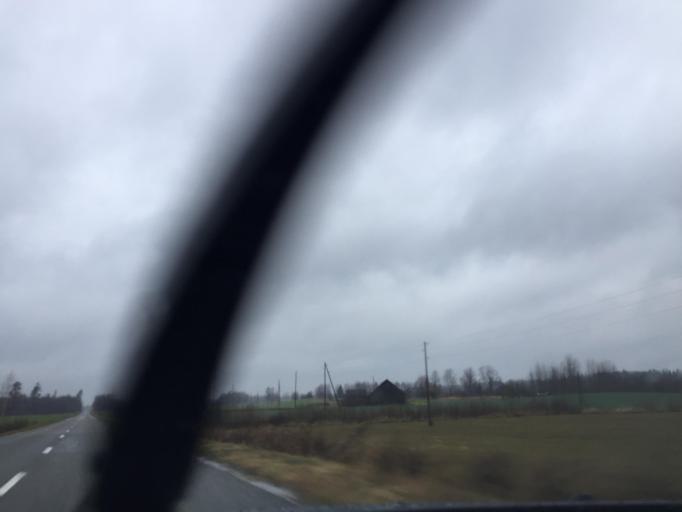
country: LV
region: Aloja
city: Staicele
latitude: 57.7601
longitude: 24.5660
